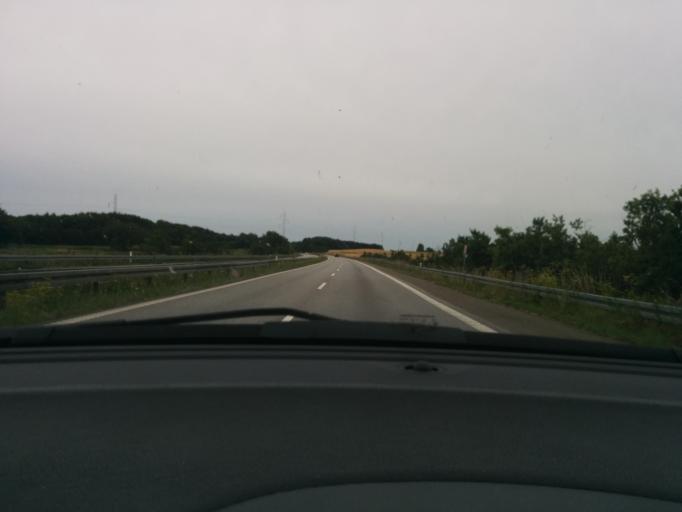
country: DK
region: Zealand
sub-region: Vordingborg Kommune
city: Orslev
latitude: 55.0985
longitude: 11.9375
